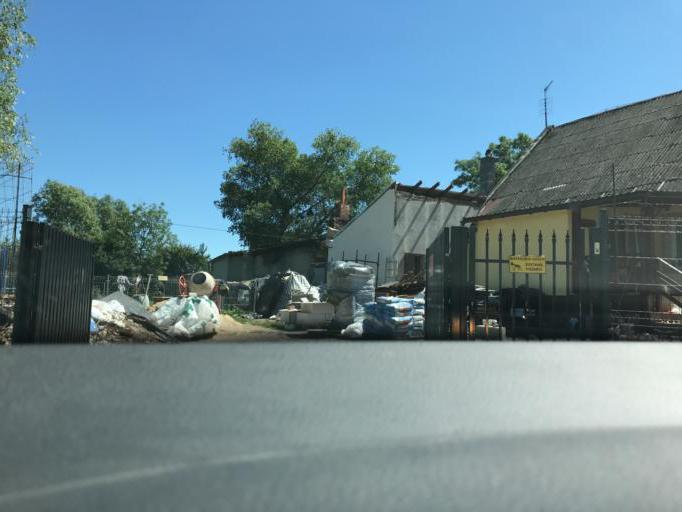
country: PL
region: Pomeranian Voivodeship
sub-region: Gdansk
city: Gdansk
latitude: 54.3352
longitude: 18.7504
